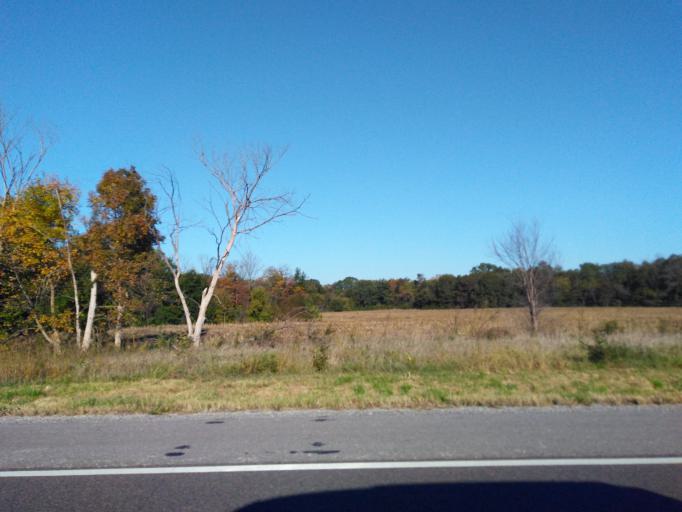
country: US
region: Illinois
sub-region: Madison County
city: Saint Jacob
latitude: 38.7733
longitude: -89.7464
